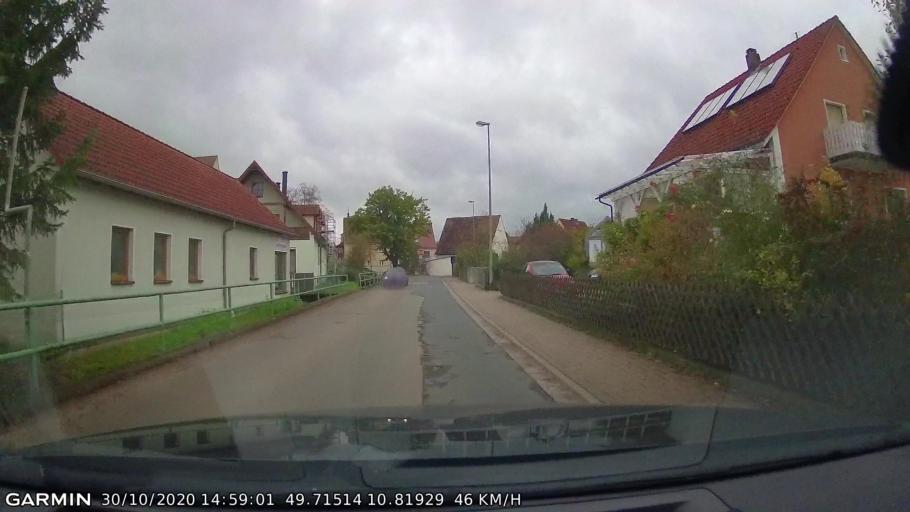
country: DE
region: Bavaria
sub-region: Regierungsbezirk Mittelfranken
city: Hochstadt an der Aisch
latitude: 49.7152
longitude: 10.8192
